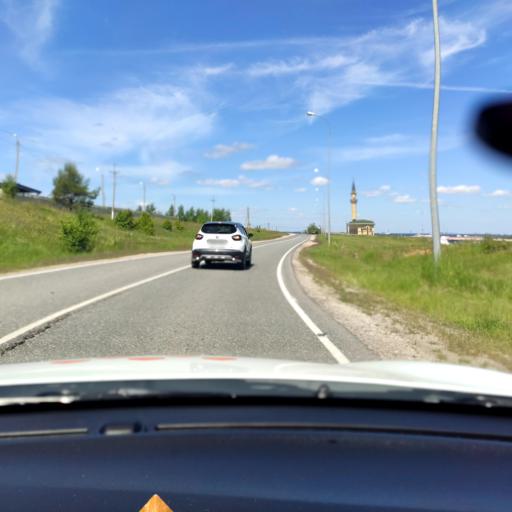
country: RU
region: Tatarstan
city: Osinovo
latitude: 55.7718
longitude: 48.8357
